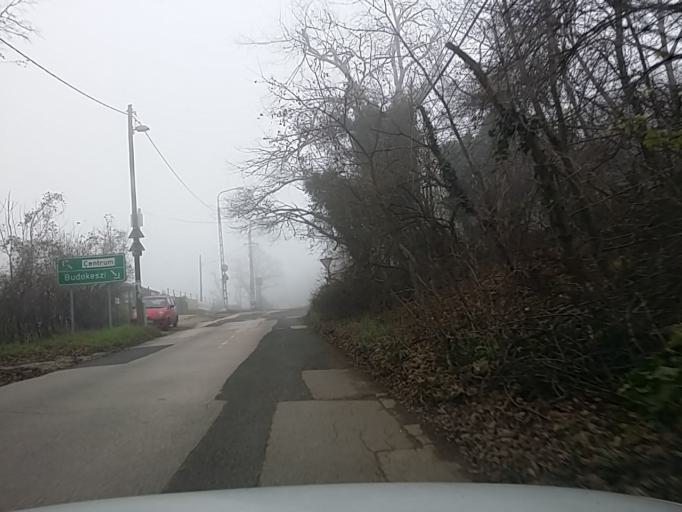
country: HU
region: Pest
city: Budakeszi
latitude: 47.5286
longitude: 18.9509
